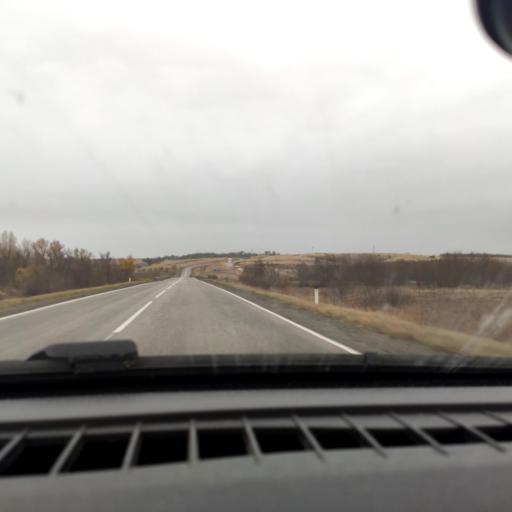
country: RU
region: Voronezj
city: Uryv-Pokrovka
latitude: 51.1290
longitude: 39.0424
